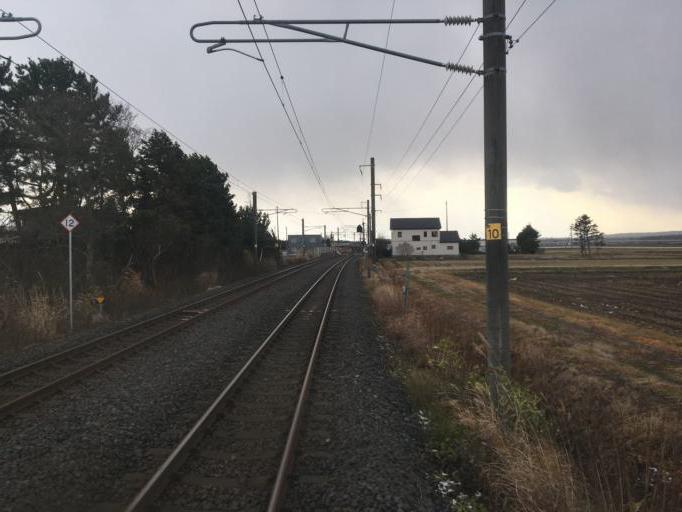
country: JP
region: Aomori
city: Aomori Shi
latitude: 40.9011
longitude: 140.6727
